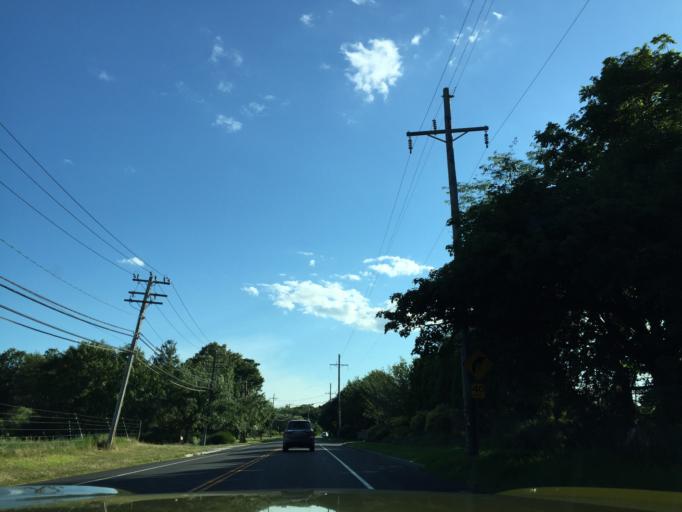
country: US
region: New York
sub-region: Suffolk County
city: Greenport
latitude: 41.1219
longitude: -72.3467
